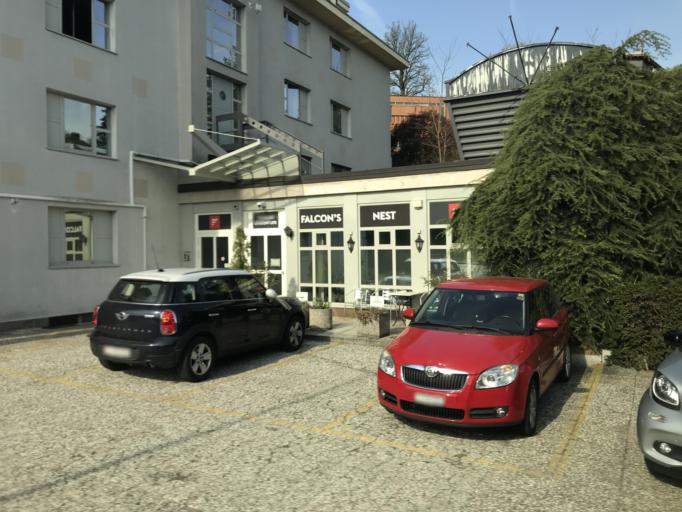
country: CH
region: Ticino
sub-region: Lugano District
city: Sorengo
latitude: 46.0005
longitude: 8.9400
